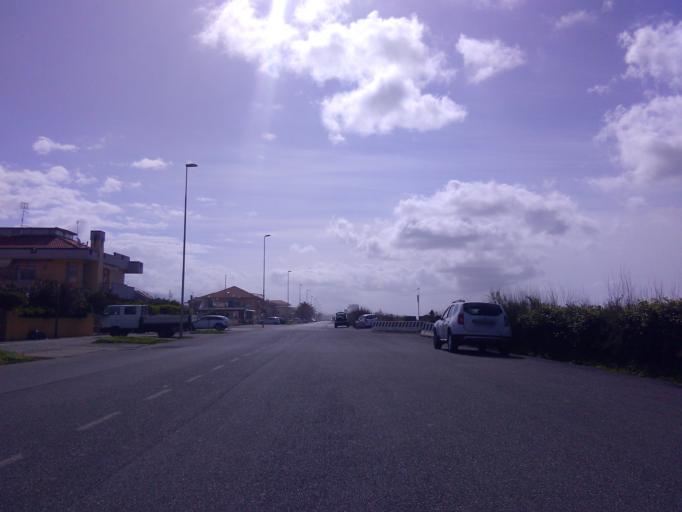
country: IT
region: Tuscany
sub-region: Provincia di Massa-Carrara
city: Marina di Carrara
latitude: 44.0314
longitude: 10.0556
